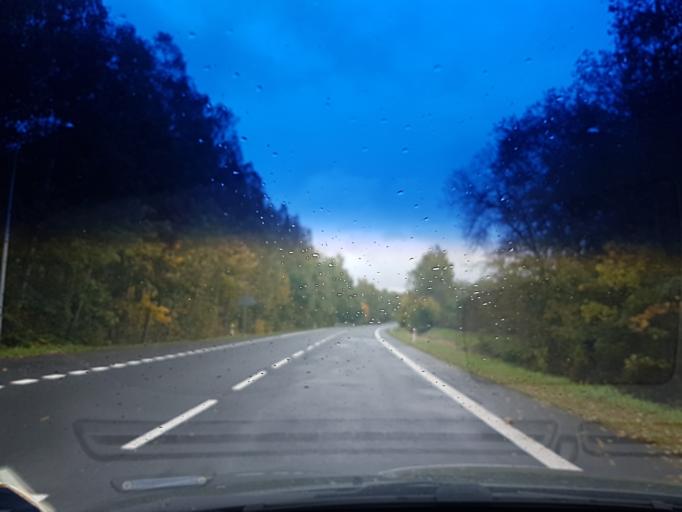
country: CZ
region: Karlovarsky
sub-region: Okres Cheb
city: Cheb
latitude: 50.0788
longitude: 12.3430
